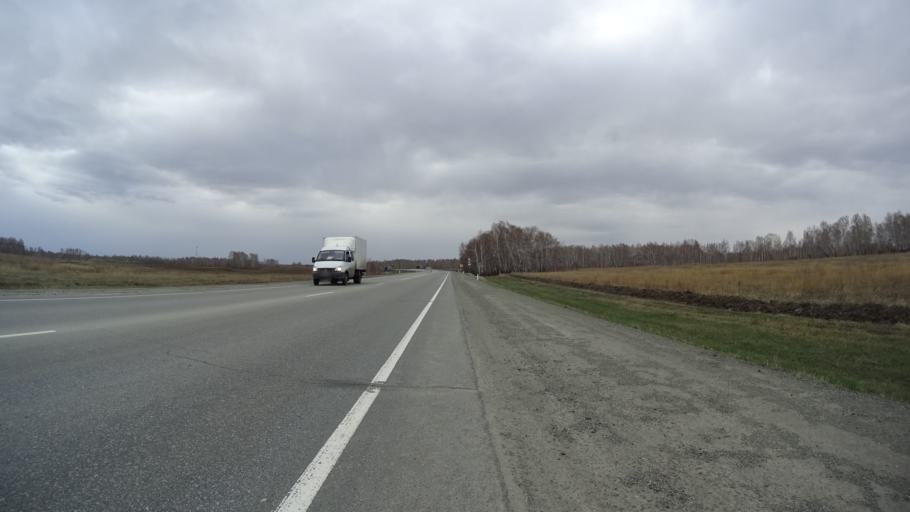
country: RU
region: Chelyabinsk
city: Yemanzhelinsk
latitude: 54.6992
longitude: 61.2515
